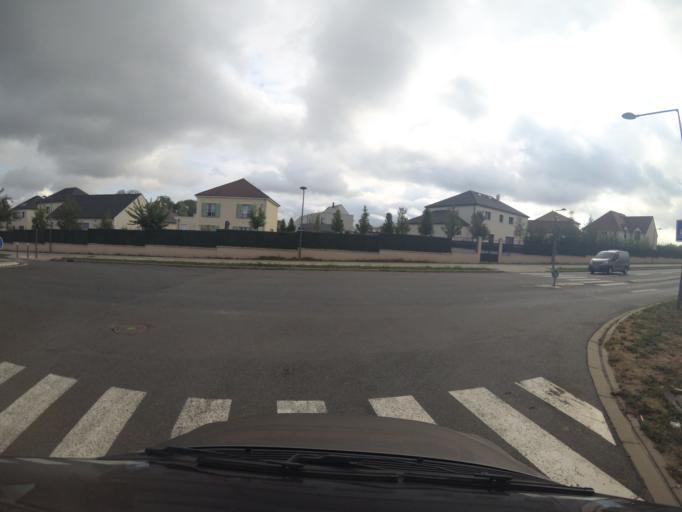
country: FR
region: Ile-de-France
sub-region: Departement de Seine-et-Marne
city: Montevrain
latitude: 48.8657
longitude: 2.7531
